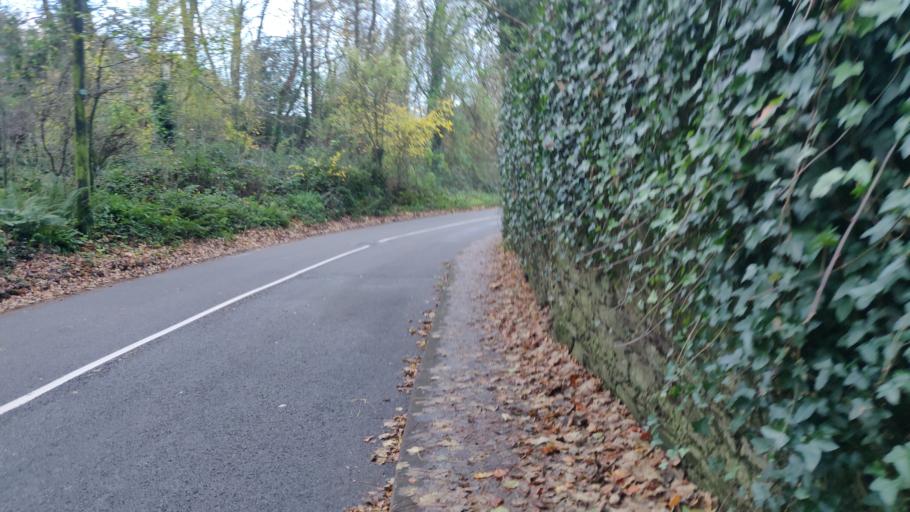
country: DE
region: North Rhine-Westphalia
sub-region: Regierungsbezirk Detmold
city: Guetersloh
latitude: 51.8732
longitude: 8.4073
